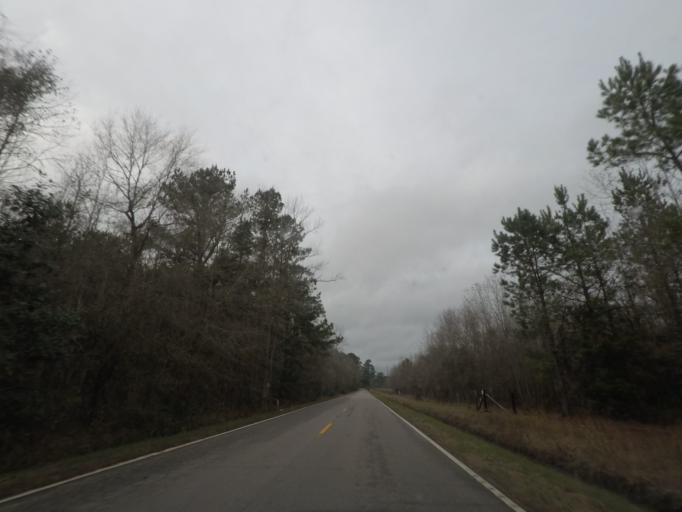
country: US
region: South Carolina
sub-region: Colleton County
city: Walterboro
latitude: 32.8867
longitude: -80.5089
